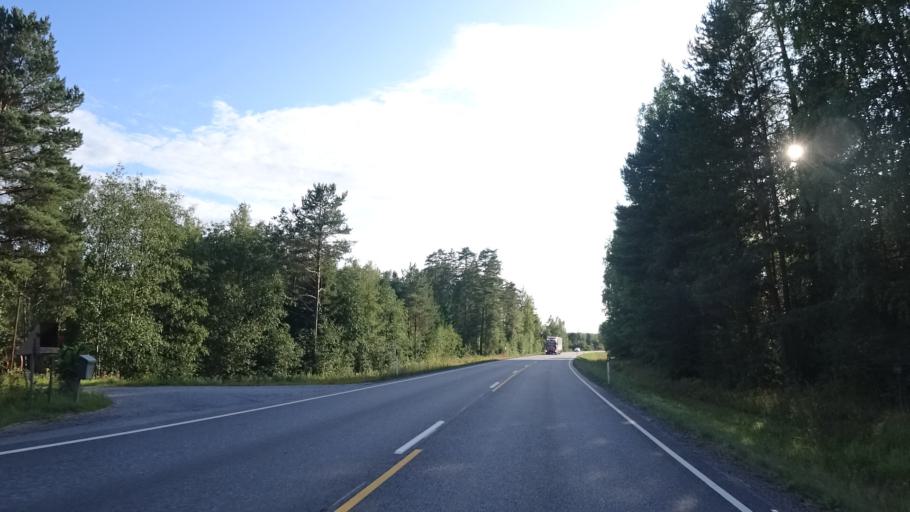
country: FI
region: South Karelia
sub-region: Imatra
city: Parikkala
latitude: 61.6101
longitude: 29.5099
